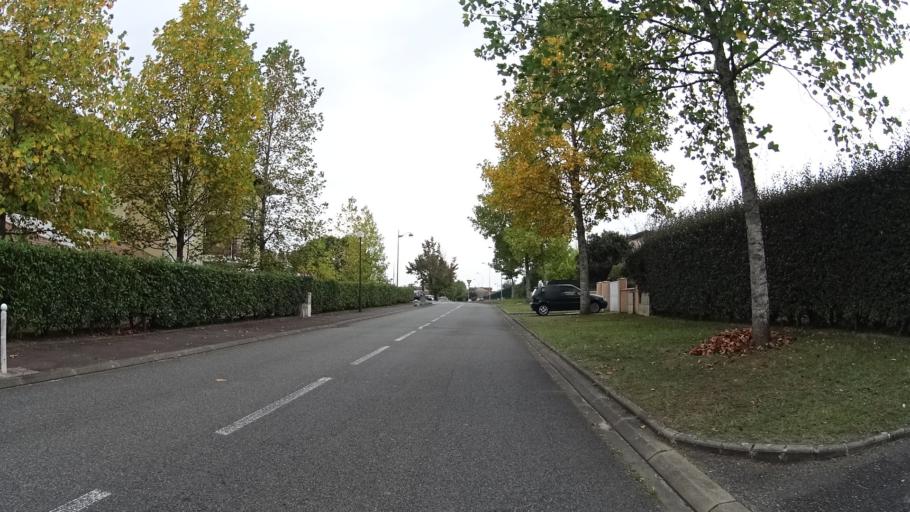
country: FR
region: Aquitaine
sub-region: Departement des Landes
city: Saint-Paul-les-Dax
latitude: 43.7286
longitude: -1.0777
